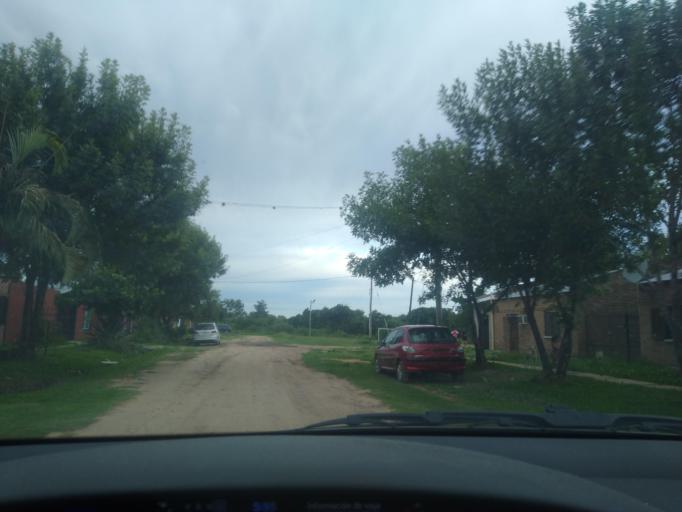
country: AR
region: Chaco
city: Barranqueras
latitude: -27.4660
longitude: -58.9460
